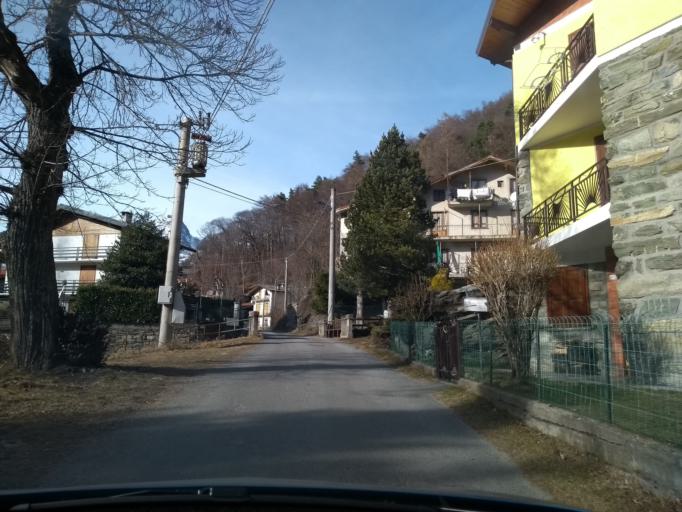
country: IT
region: Piedmont
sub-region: Provincia di Torino
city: Ala di Stura
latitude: 45.3145
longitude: 7.3185
